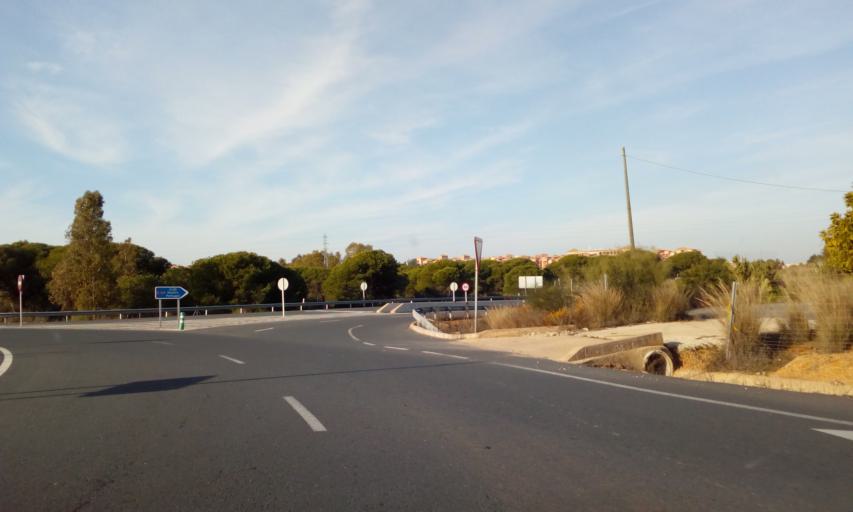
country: ES
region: Andalusia
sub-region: Provincia de Huelva
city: Lepe
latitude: 37.2139
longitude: -7.2178
